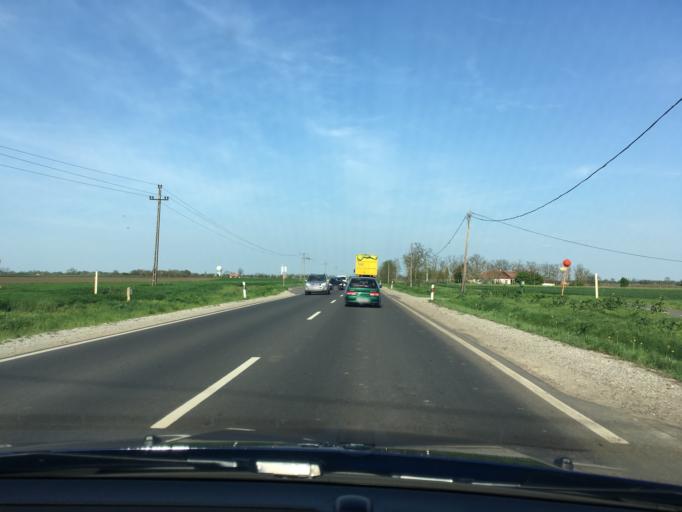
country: HU
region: Bekes
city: Ujkigyos
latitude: 46.6715
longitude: 20.9934
